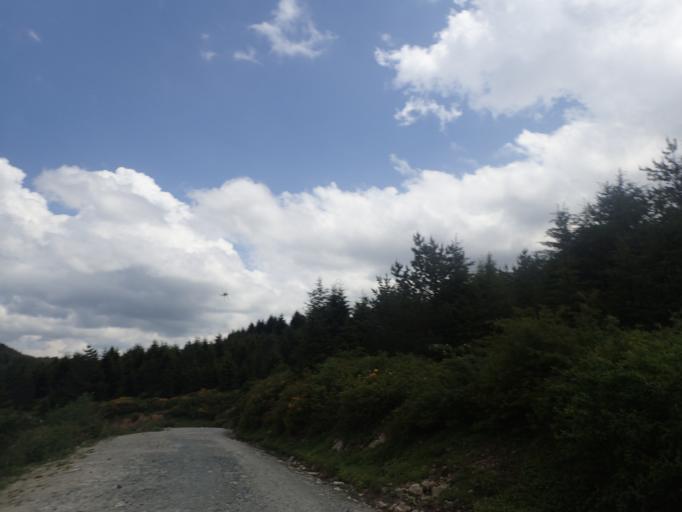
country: TR
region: Ordu
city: Topcam
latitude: 40.6823
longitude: 37.9412
